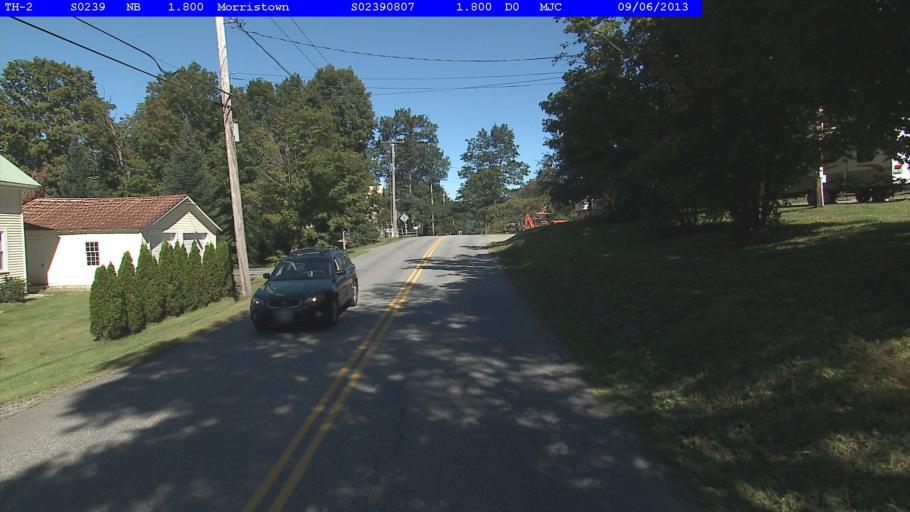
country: US
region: Vermont
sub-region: Lamoille County
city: Hyde Park
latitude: 44.5796
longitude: -72.6127
